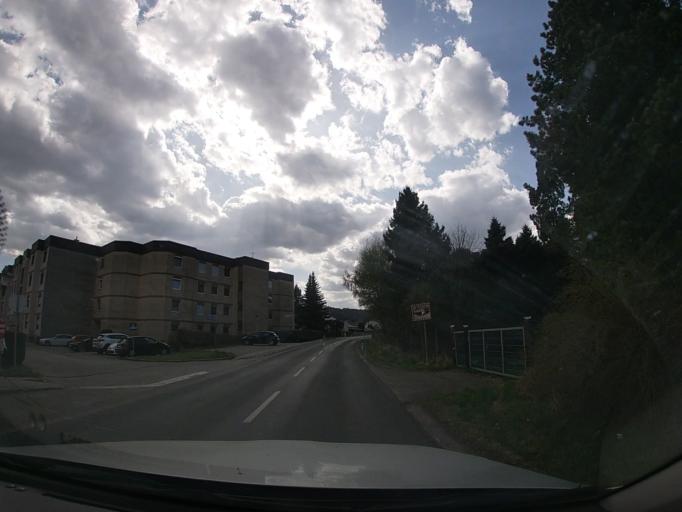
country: AT
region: Styria
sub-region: Politischer Bezirk Murtal
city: Poels
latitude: 47.2234
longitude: 14.5879
